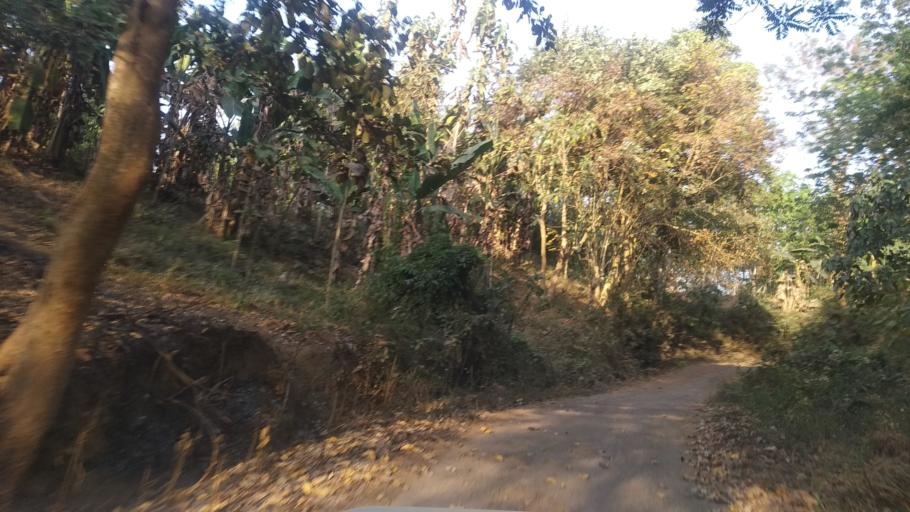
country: IN
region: Tripura
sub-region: West Tripura
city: Sonamura
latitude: 23.4442
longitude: 91.3647
